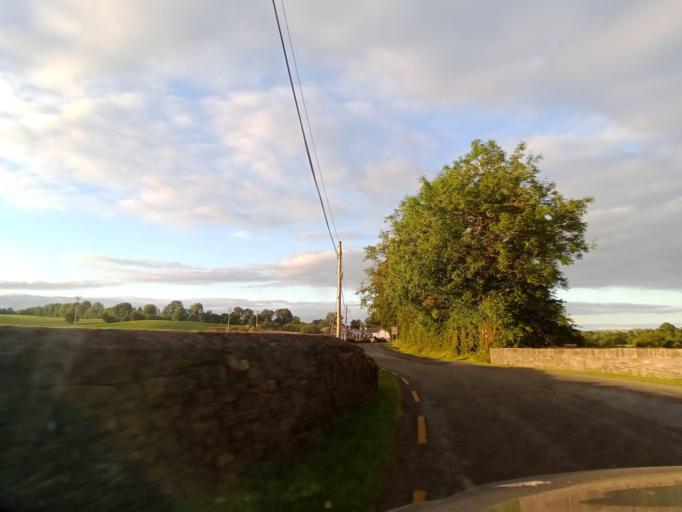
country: IE
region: Leinster
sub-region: Kilkenny
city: Castlecomer
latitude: 52.8274
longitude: -7.2054
